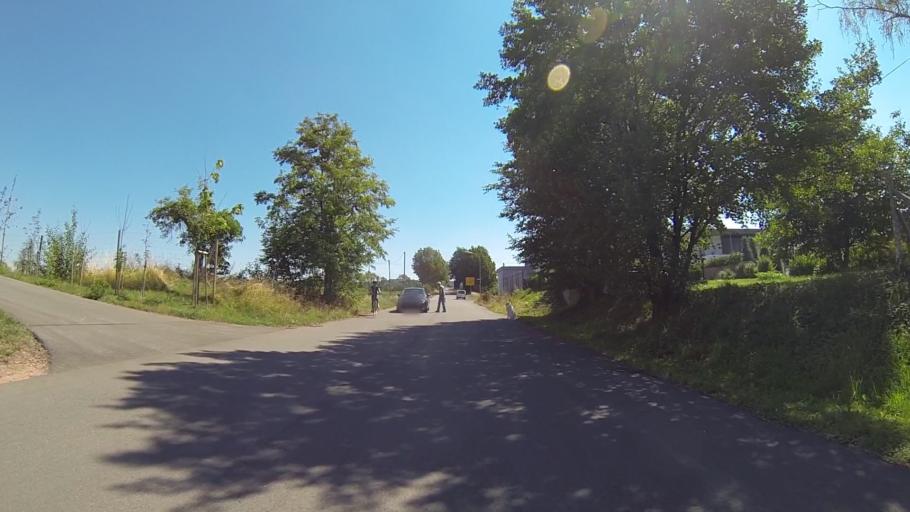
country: LU
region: Grevenmacher
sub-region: Canton de Remich
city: Remich
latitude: 49.5084
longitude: 6.3681
